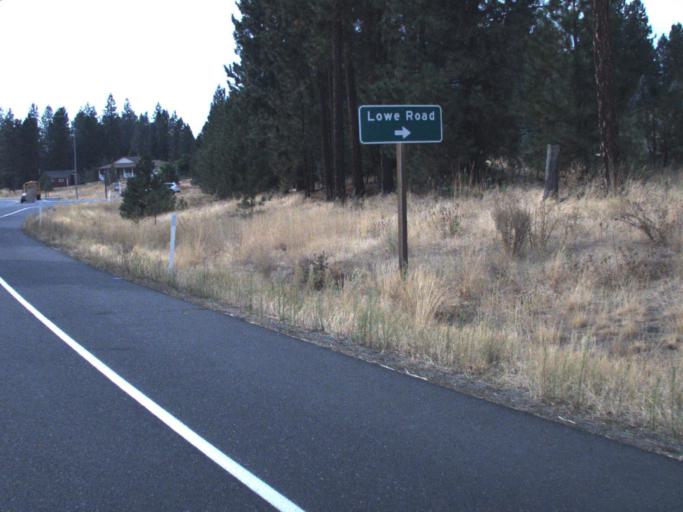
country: US
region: Washington
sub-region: Spokane County
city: Mead
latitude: 47.7873
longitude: -117.3372
